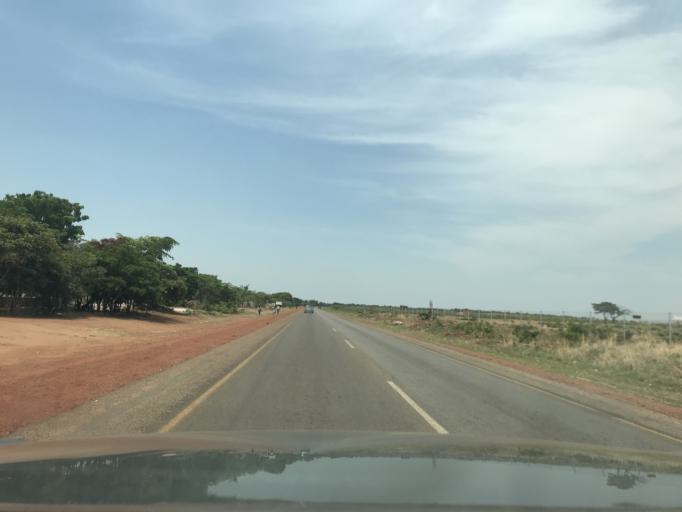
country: ZM
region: Northern
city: Kasama
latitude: -10.2189
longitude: 31.1404
